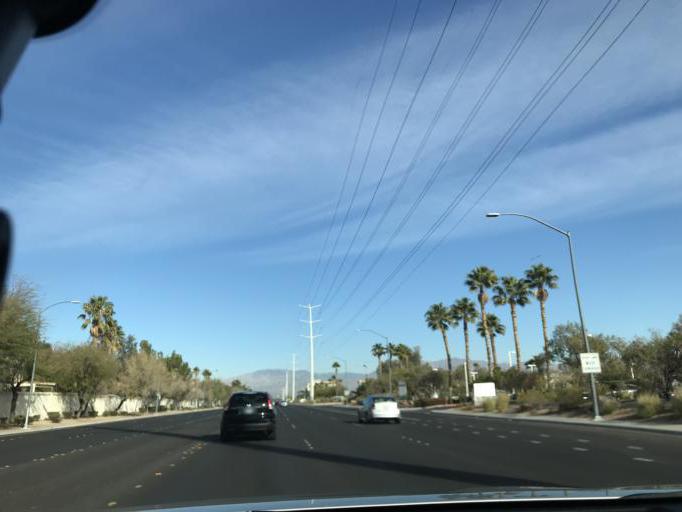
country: US
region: Nevada
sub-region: Clark County
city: Spring Valley
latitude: 36.2051
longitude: -115.2606
